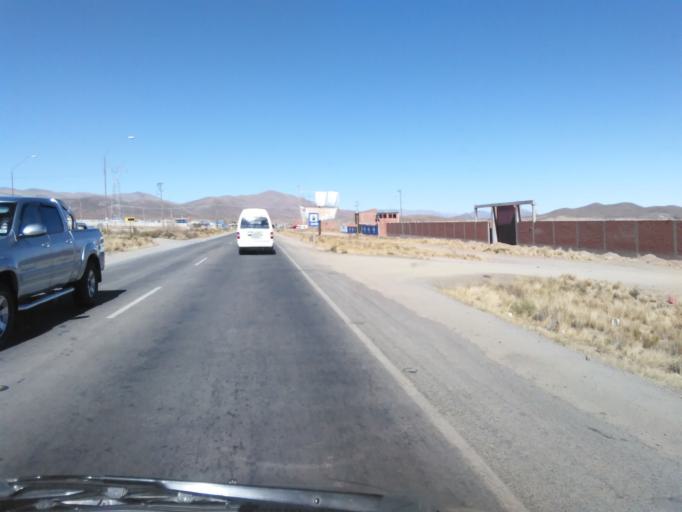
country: BO
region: Oruro
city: Oruro
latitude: -18.0153
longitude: -67.0335
